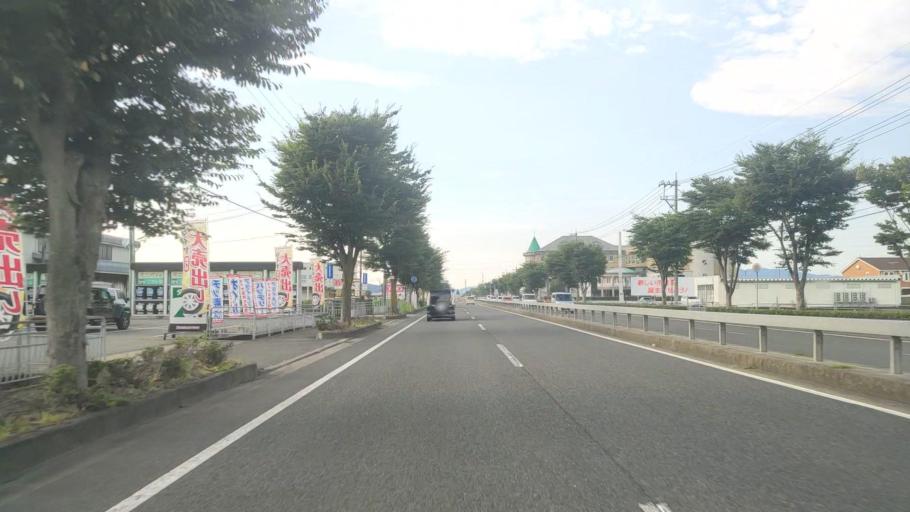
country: JP
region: Fukui
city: Takefu
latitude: 35.9141
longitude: 136.1915
